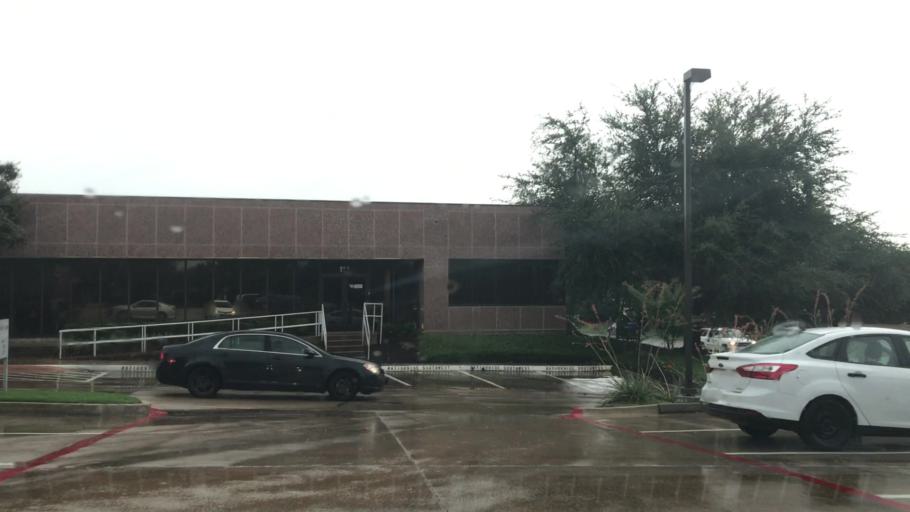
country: US
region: Texas
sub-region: Dallas County
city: Coppell
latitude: 32.8932
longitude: -96.9844
